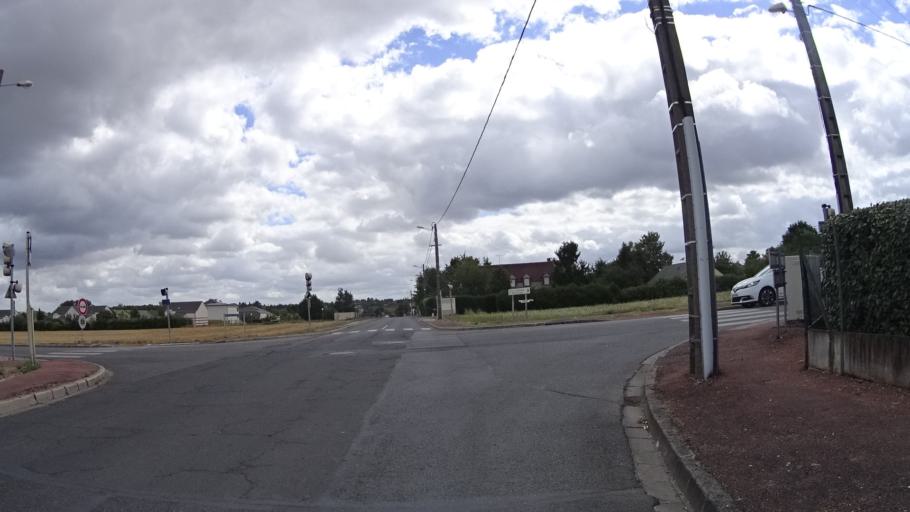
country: FR
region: Centre
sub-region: Departement du Loiret
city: Villemandeur
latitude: 47.9811
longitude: 2.7161
